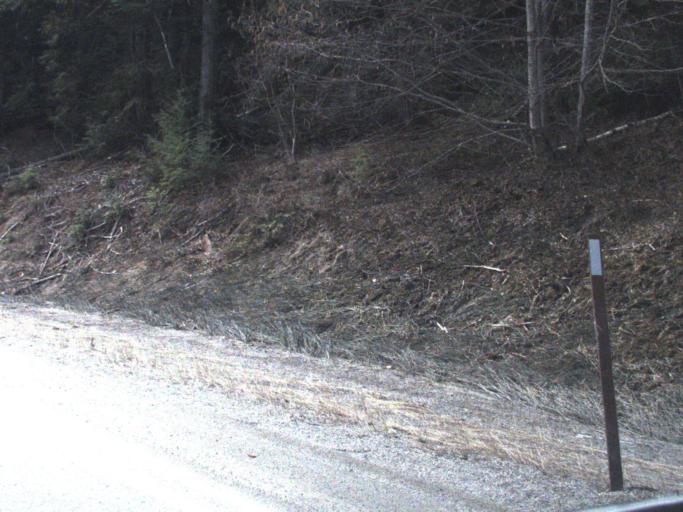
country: US
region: Washington
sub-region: Stevens County
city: Chewelah
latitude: 48.5614
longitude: -117.3521
